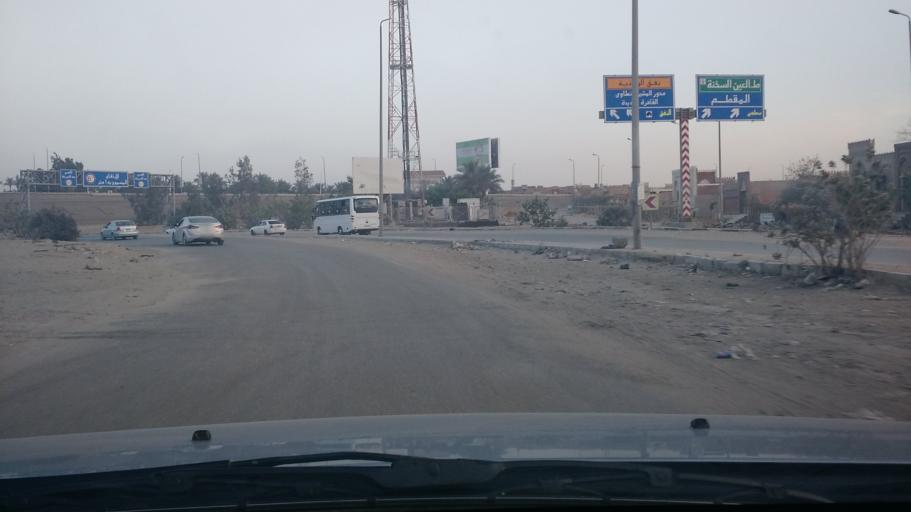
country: EG
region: Muhafazat al Qahirah
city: Cairo
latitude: 30.0251
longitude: 31.3537
